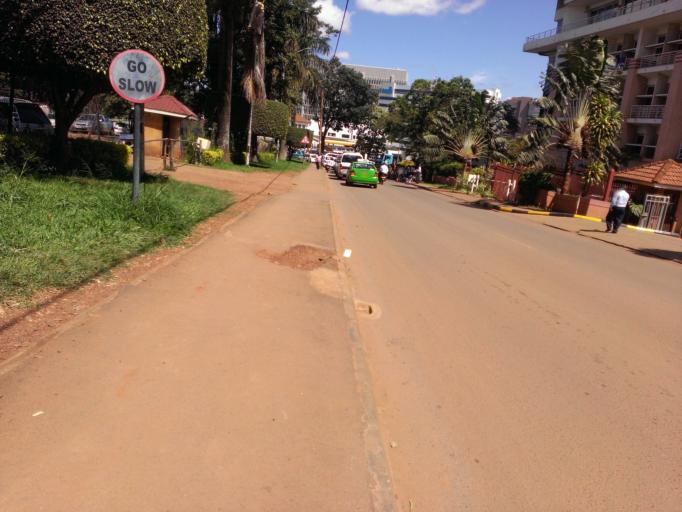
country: UG
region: Central Region
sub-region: Kampala District
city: Kampala
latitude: 0.3170
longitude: 32.5803
